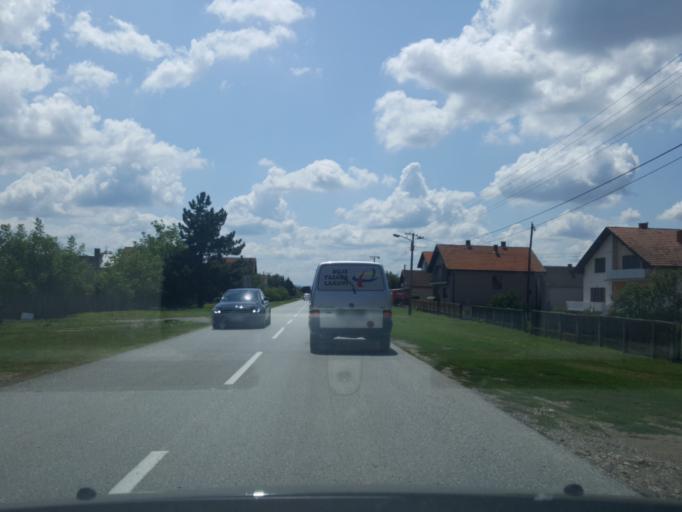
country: RS
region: Central Serbia
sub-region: Macvanski Okrug
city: Bogatic
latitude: 44.8278
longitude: 19.4782
